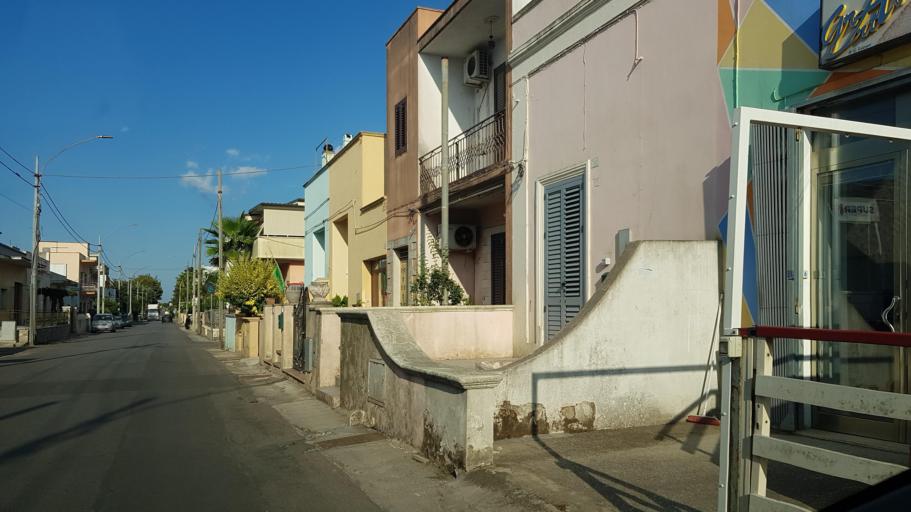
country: IT
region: Apulia
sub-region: Provincia di Lecce
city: Miggiano
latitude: 39.9656
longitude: 18.3133
